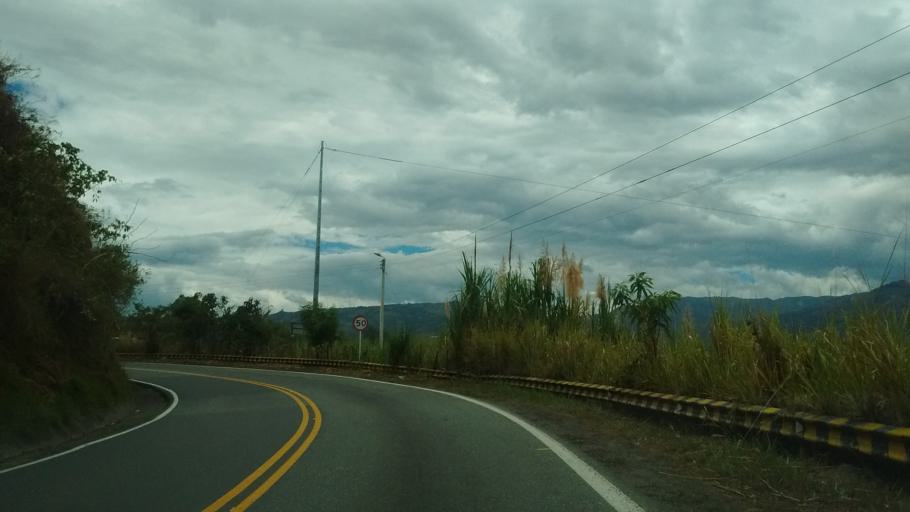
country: CO
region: Cauca
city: La Sierra
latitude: 2.2272
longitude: -76.7959
